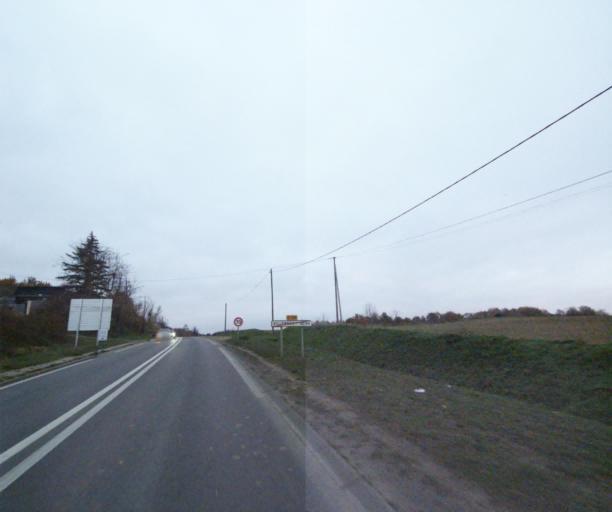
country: FR
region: Ile-de-France
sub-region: Departement des Yvelines
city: Villennes-sur-Seine
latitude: 48.9420
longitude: 1.9782
